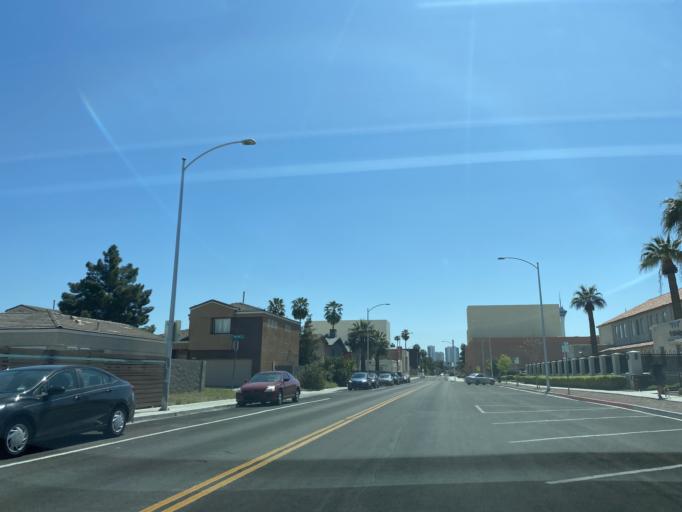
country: US
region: Nevada
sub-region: Clark County
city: Las Vegas
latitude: 36.1648
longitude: -115.1377
